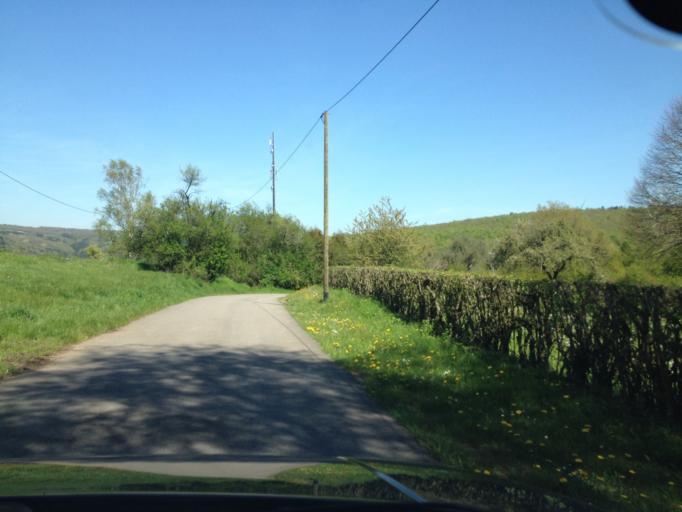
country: DE
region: Saarland
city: Hangard
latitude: 49.3772
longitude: 7.2202
